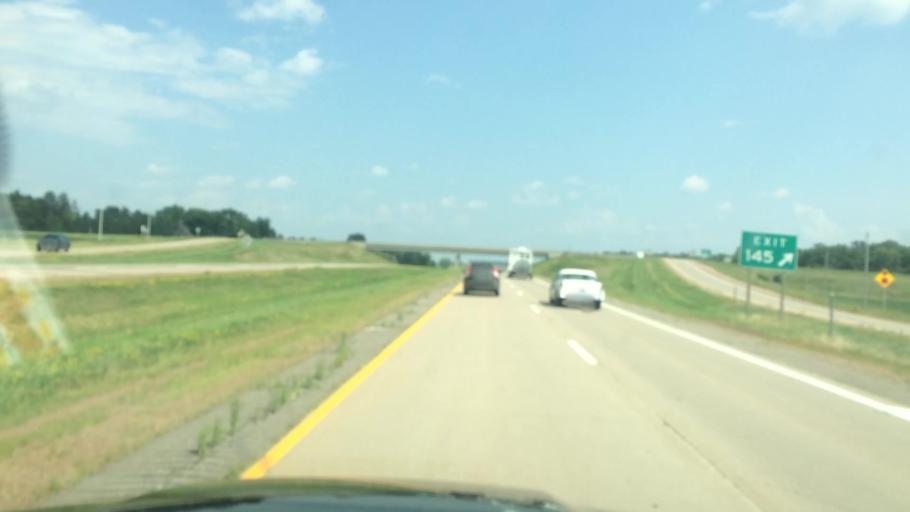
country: US
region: Wisconsin
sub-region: Marathon County
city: Athens
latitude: 44.9453
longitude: -90.0832
